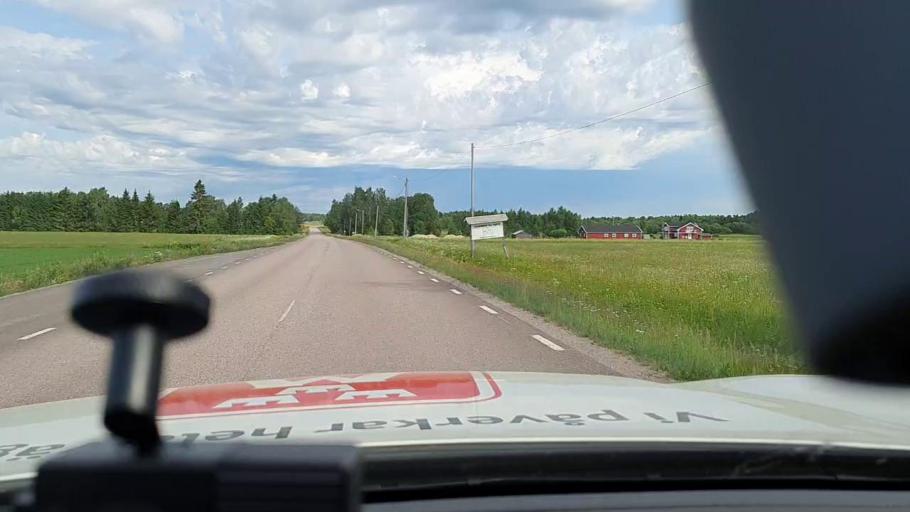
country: SE
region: Norrbotten
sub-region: Bodens Kommun
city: Saevast
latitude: 65.6946
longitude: 21.7803
